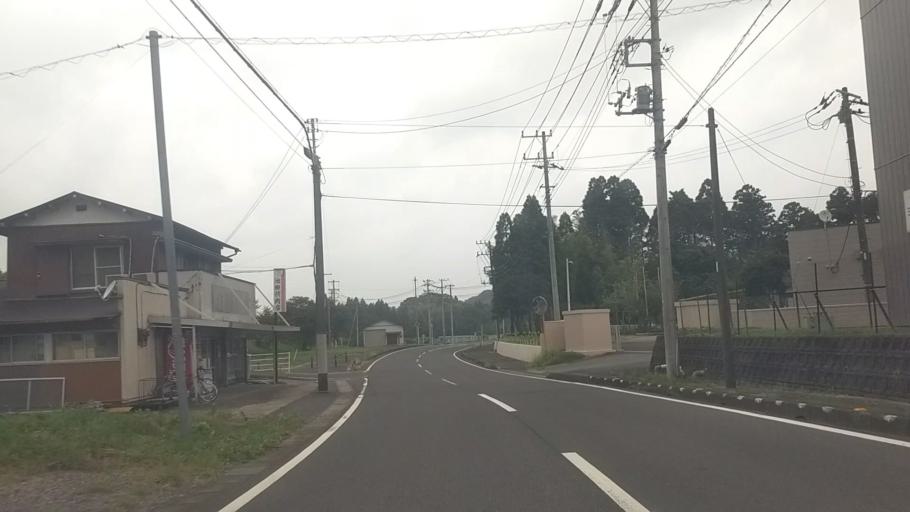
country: JP
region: Chiba
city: Ohara
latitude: 35.2656
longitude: 140.2546
